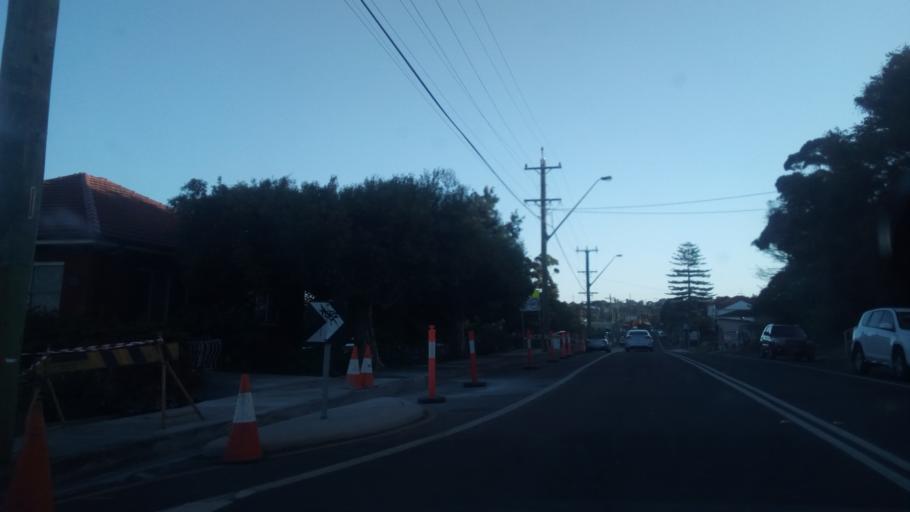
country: AU
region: New South Wales
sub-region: Wollongong
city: Cringila
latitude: -34.4706
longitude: 150.8716
